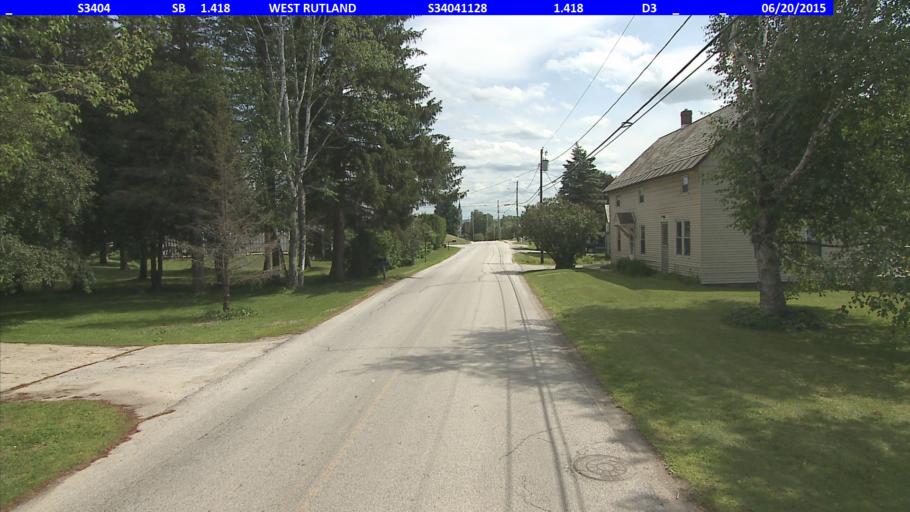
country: US
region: Vermont
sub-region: Rutland County
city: West Rutland
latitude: 43.6116
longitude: -73.0506
